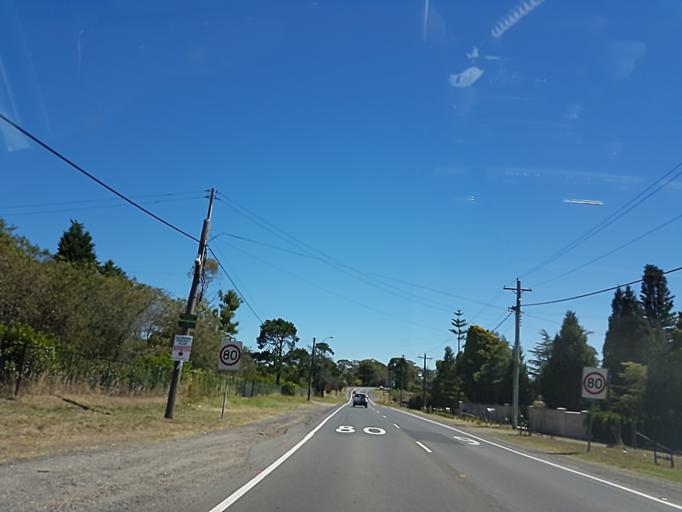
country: AU
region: New South Wales
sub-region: The Hills Shire
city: Kenthurst
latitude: -33.6405
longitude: 151.0224
